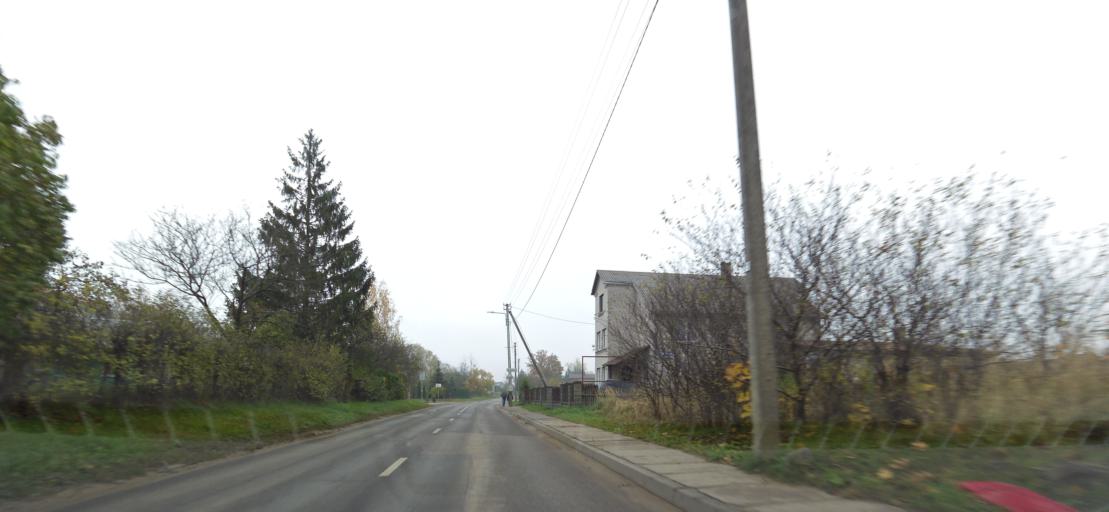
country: LT
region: Vilnius County
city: Rasos
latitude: 54.6601
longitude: 25.3578
